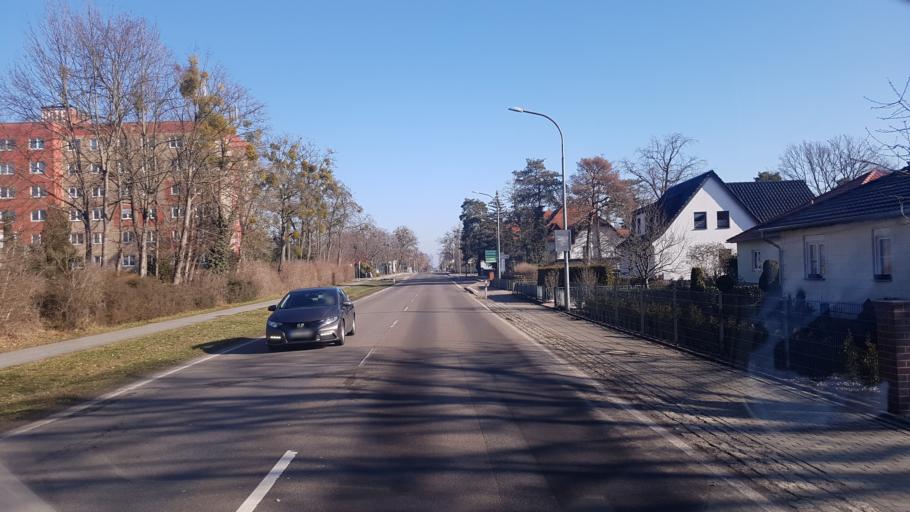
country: DE
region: Brandenburg
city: Senftenberg
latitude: 51.5011
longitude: 13.9650
